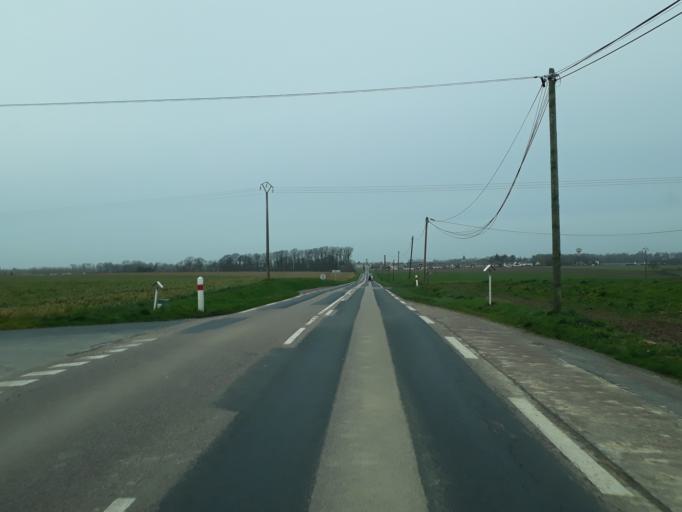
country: FR
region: Haute-Normandie
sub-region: Departement de la Seine-Maritime
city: Breaute
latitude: 49.6150
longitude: 0.4078
